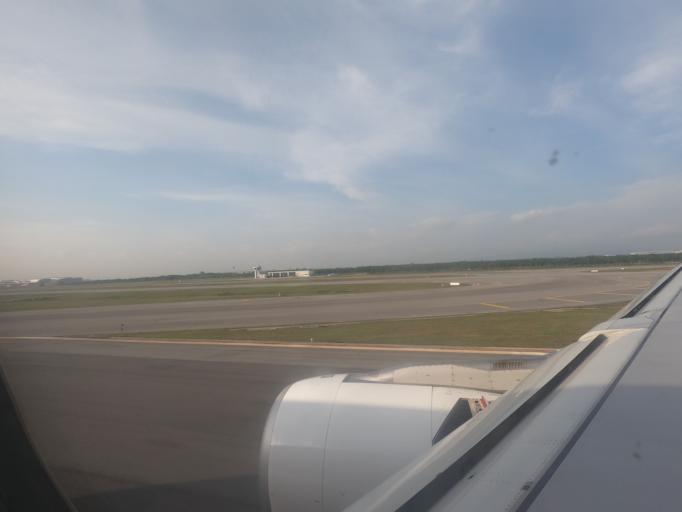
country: MY
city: Sungai Pelek New Village
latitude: 2.7206
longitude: 101.6893
